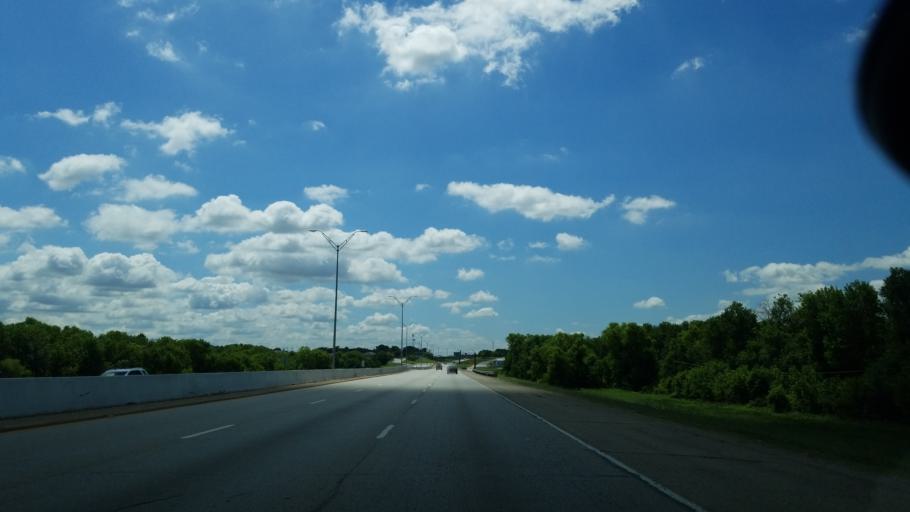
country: US
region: Texas
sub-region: Dallas County
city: Hutchins
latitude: 32.7391
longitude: -96.7190
